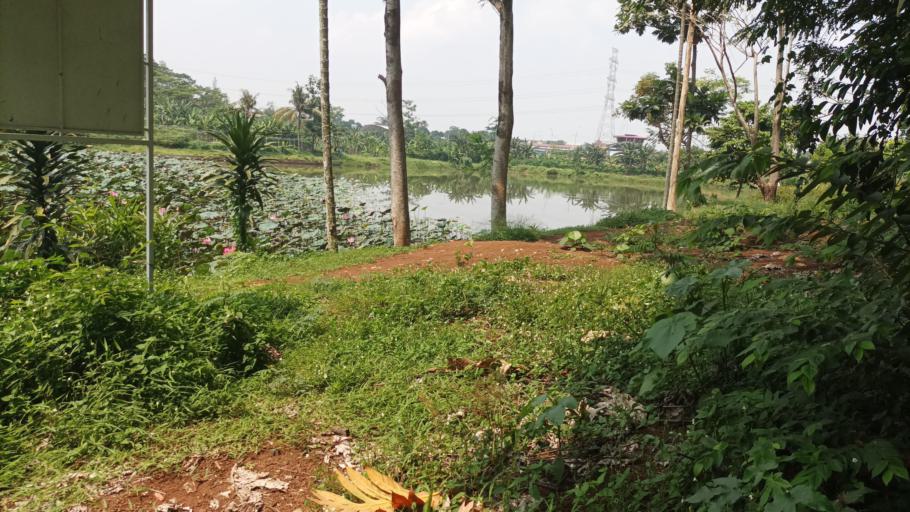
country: ID
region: West Java
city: Depok
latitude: -6.4237
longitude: 106.8598
